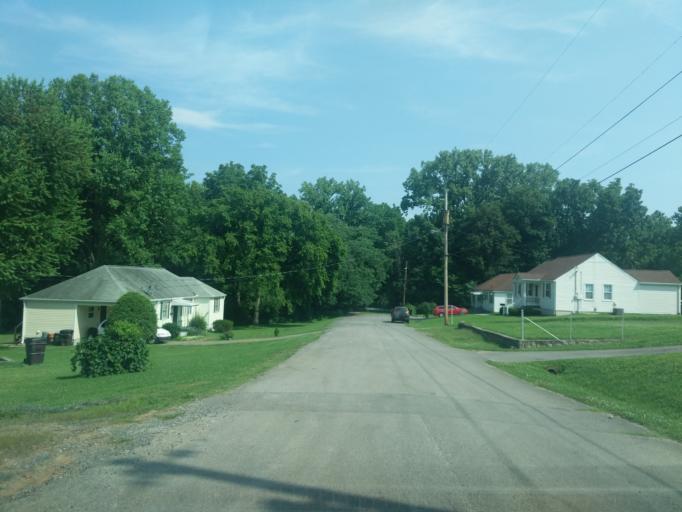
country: US
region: Tennessee
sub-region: Davidson County
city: Lakewood
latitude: 36.2630
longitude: -86.6571
